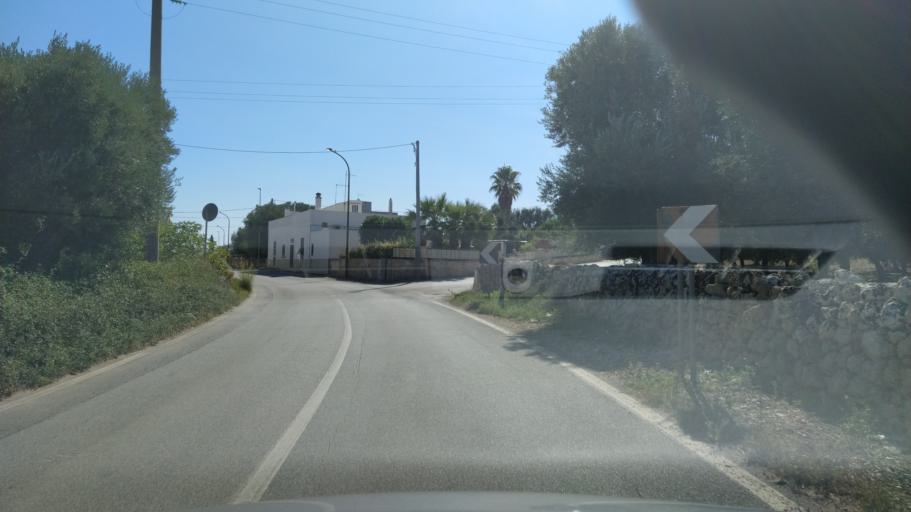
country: IT
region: Apulia
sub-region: Provincia di Brindisi
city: Fasano
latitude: 40.8973
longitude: 17.3525
